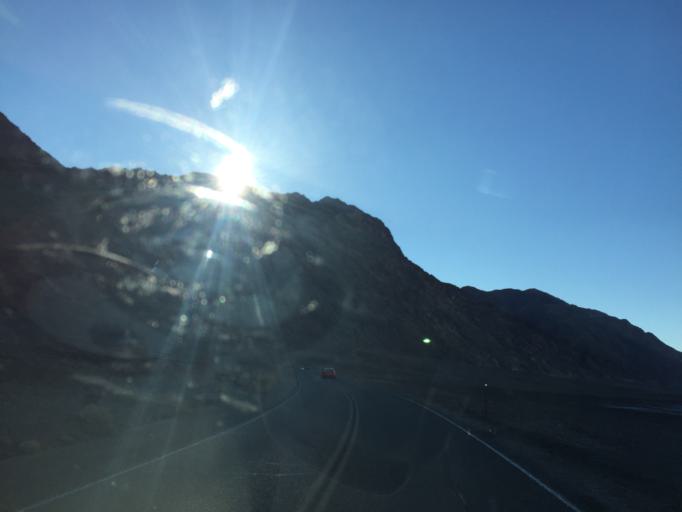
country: US
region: Nevada
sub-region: Nye County
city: Beatty
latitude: 36.1919
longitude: -116.7718
